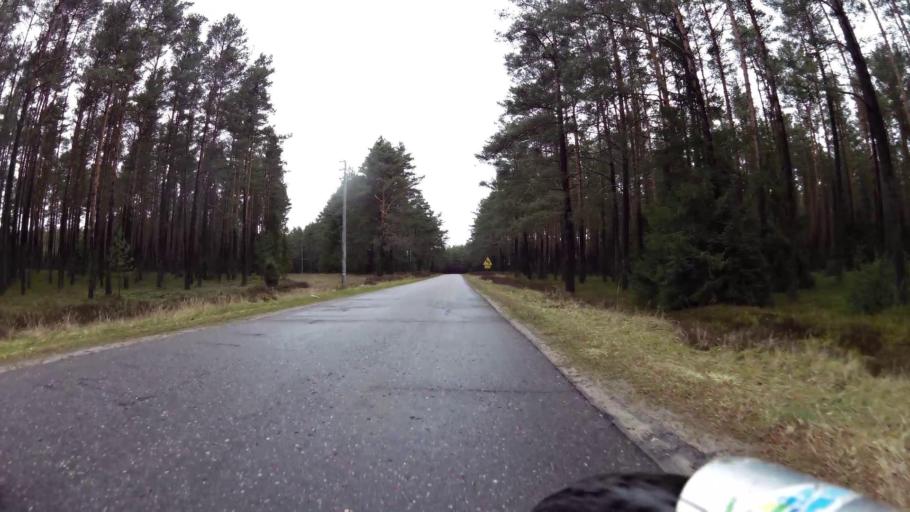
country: PL
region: Pomeranian Voivodeship
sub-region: Powiat bytowski
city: Borzytuchom
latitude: 54.2619
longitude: 17.3665
